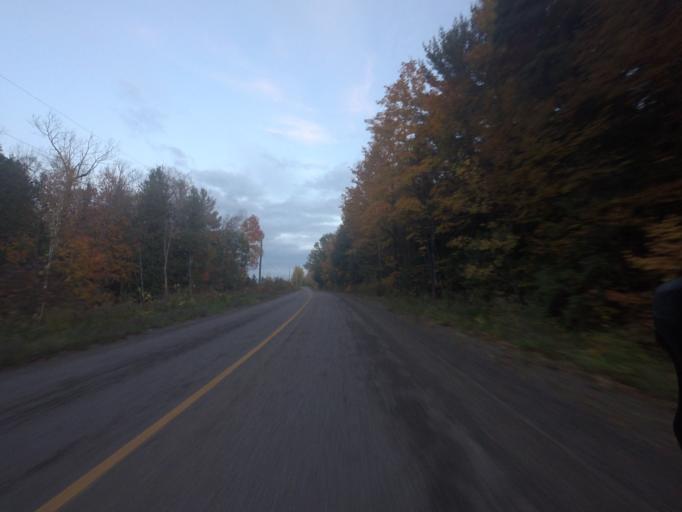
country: CA
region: Ontario
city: Renfrew
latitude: 45.3501
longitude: -76.9472
